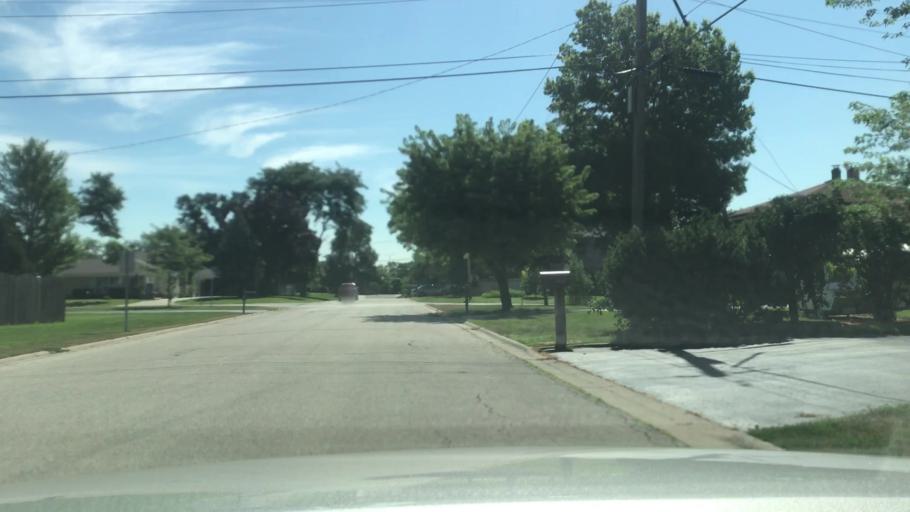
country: US
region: Illinois
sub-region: Cook County
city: Hickory Hills
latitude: 41.7366
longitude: -87.8269
